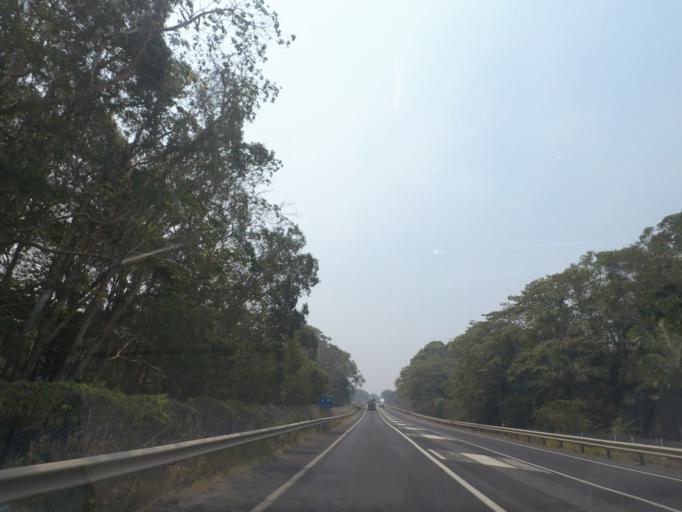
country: AU
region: New South Wales
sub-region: Ballina
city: Ballina
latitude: -28.9258
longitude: 153.4757
